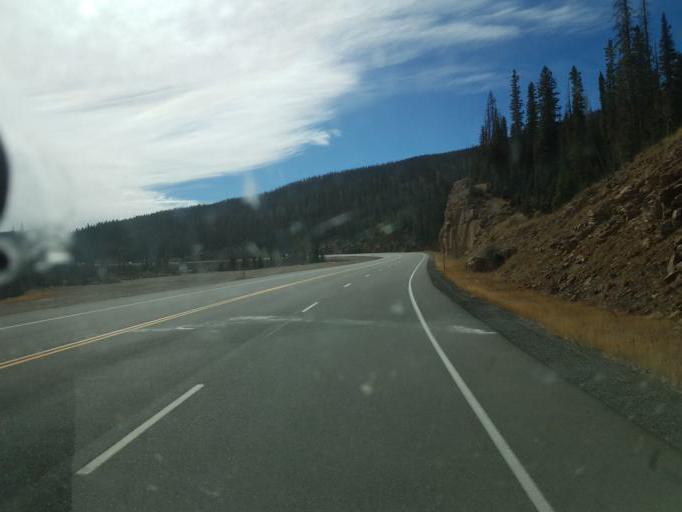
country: US
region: Colorado
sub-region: Archuleta County
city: Pagosa Springs
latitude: 37.5082
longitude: -106.7735
